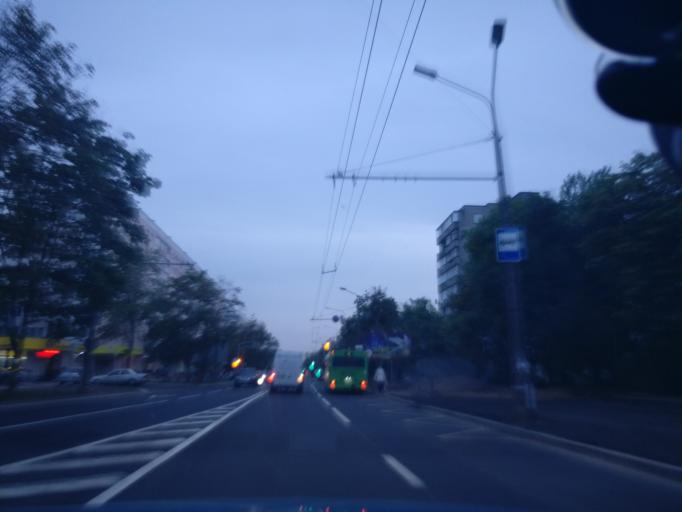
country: BY
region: Minsk
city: Minsk
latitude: 53.9257
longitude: 27.5824
